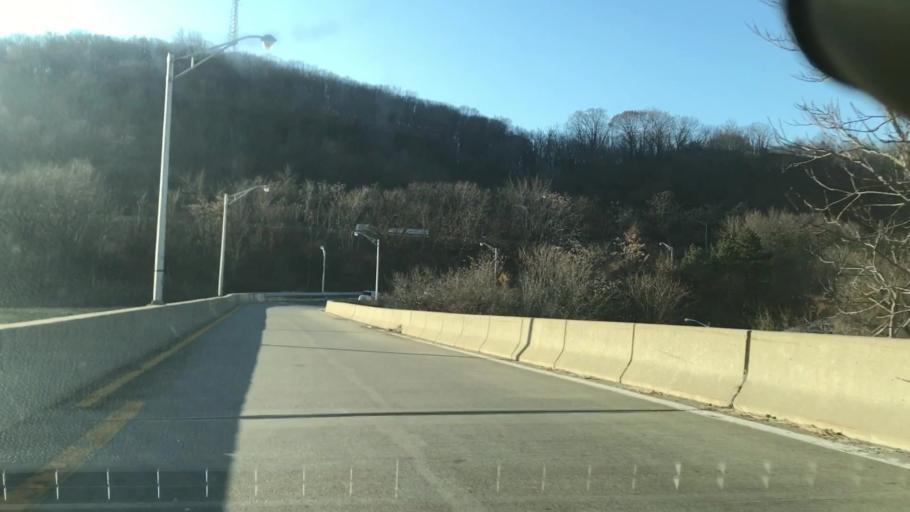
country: US
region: New Jersey
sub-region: Passaic County
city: Paterson
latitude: 40.9101
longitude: -74.1766
